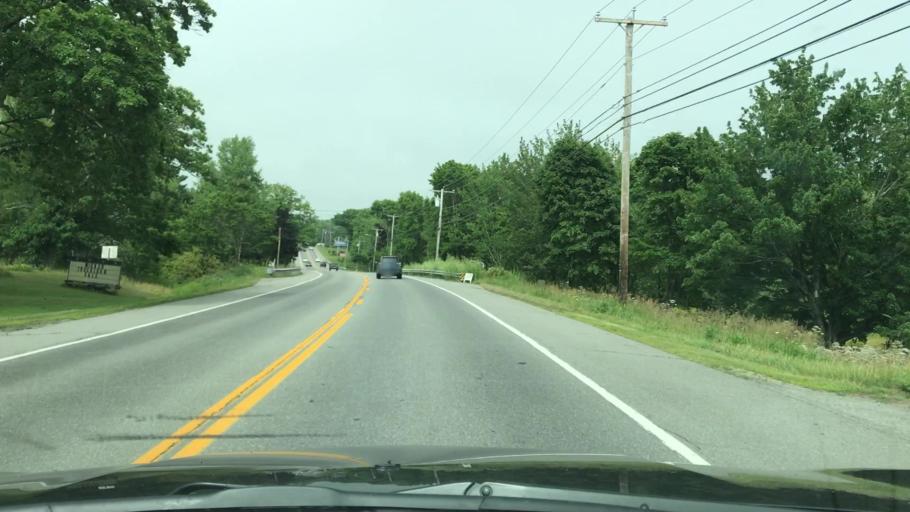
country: US
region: Maine
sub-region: Waldo County
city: Belfast
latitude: 44.4385
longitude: -68.9391
